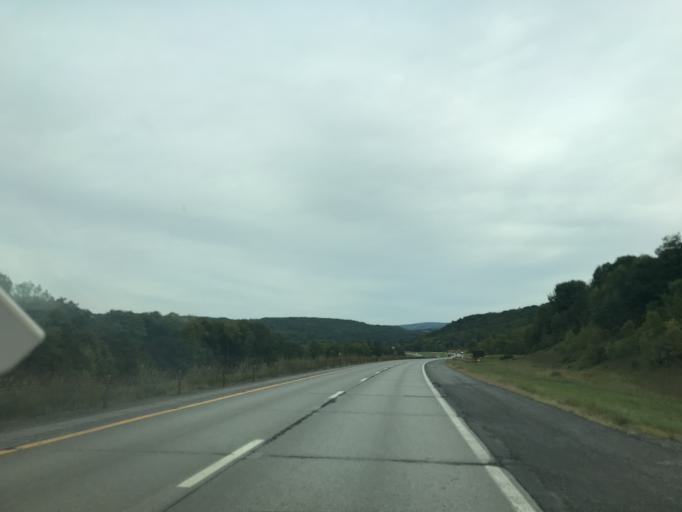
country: US
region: New York
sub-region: Otsego County
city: Worcester
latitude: 42.6498
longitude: -74.6274
